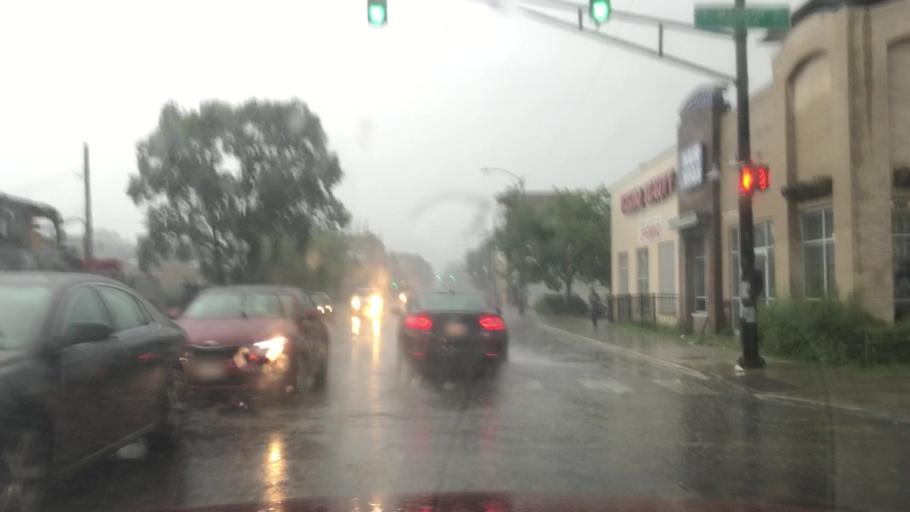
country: US
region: Illinois
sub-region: Cook County
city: Oak Park
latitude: 41.8803
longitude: -87.7550
